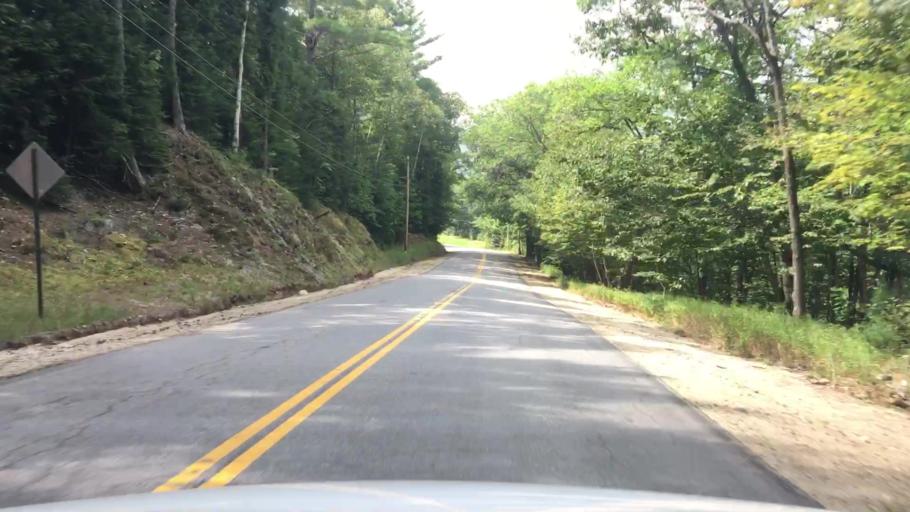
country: US
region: Maine
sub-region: Oxford County
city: Rumford
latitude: 44.5477
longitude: -70.6832
